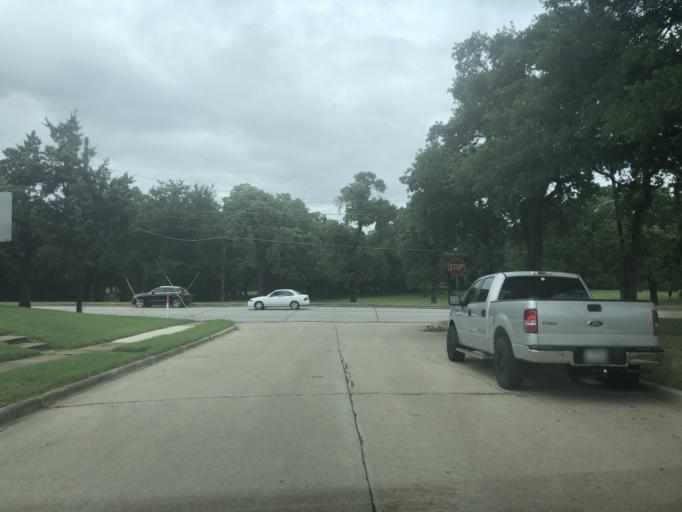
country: US
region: Texas
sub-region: Dallas County
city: Irving
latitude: 32.8015
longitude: -96.9436
